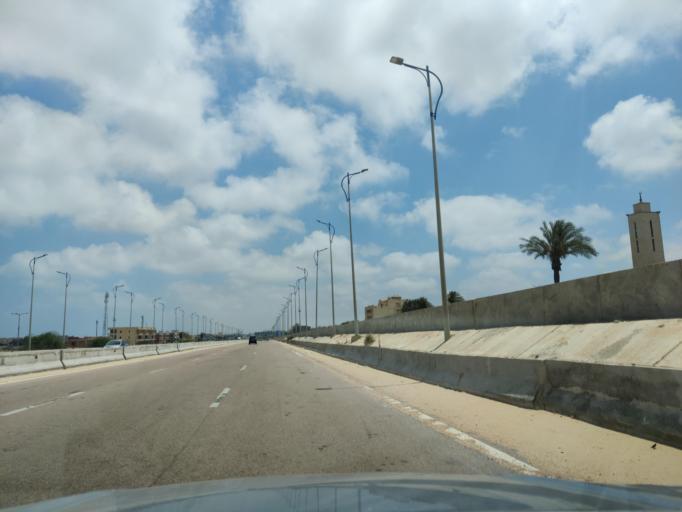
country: EG
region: Alexandria
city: Alexandria
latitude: 30.9721
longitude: 29.5654
